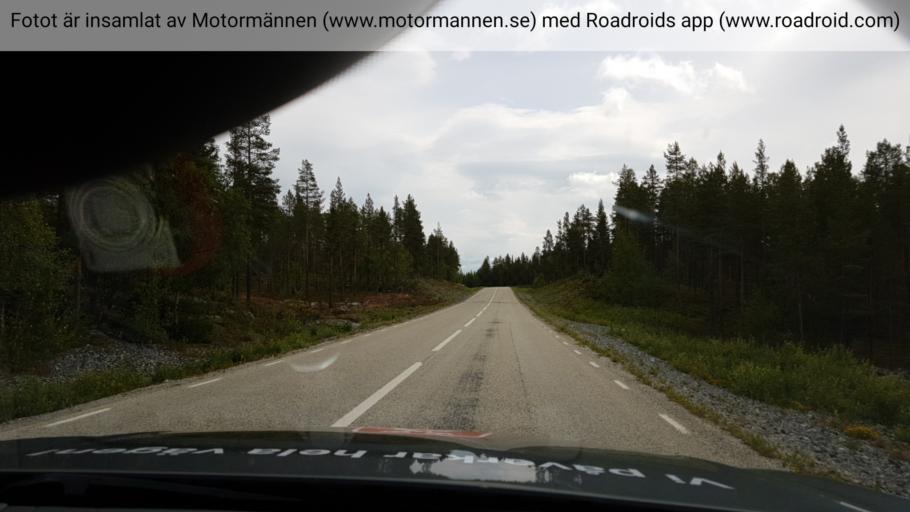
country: SE
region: Jaemtland
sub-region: Are Kommun
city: Jarpen
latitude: 62.8406
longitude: 13.4113
